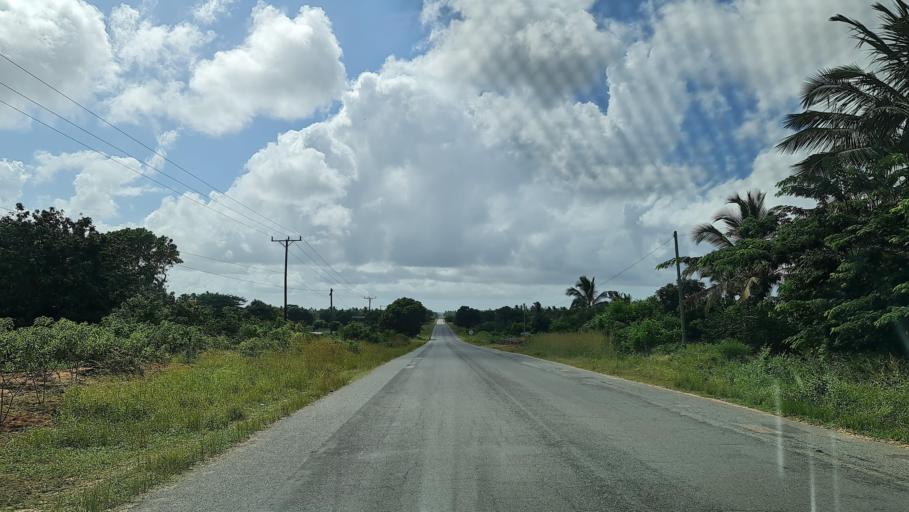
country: MZ
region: Gaza
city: Manjacaze
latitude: -24.6755
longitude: 34.5835
